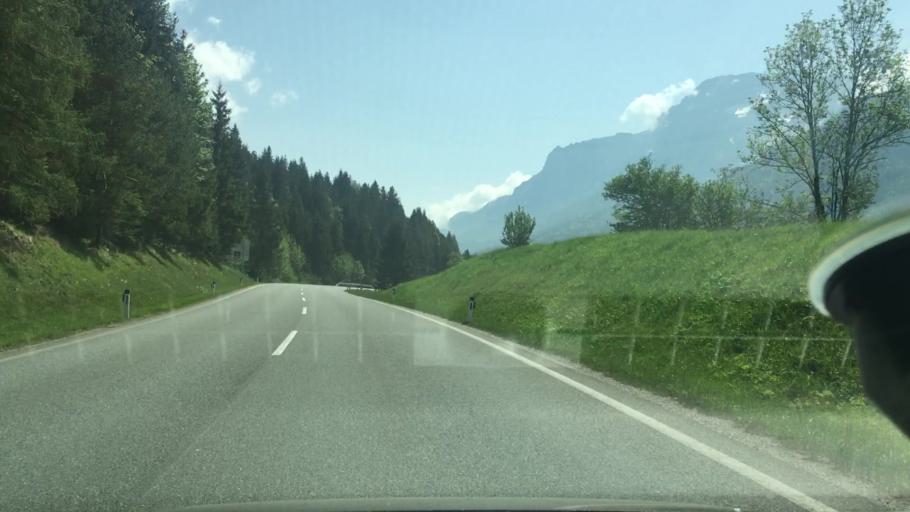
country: AT
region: Tyrol
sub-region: Politischer Bezirk Kitzbuhel
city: Waidring
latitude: 47.5882
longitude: 12.5692
